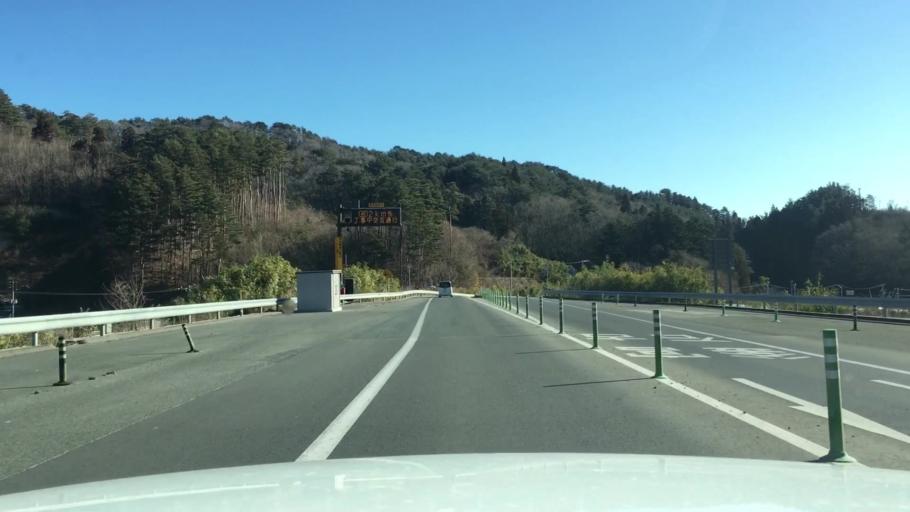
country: JP
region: Iwate
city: Yamada
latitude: 39.4803
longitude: 141.9515
